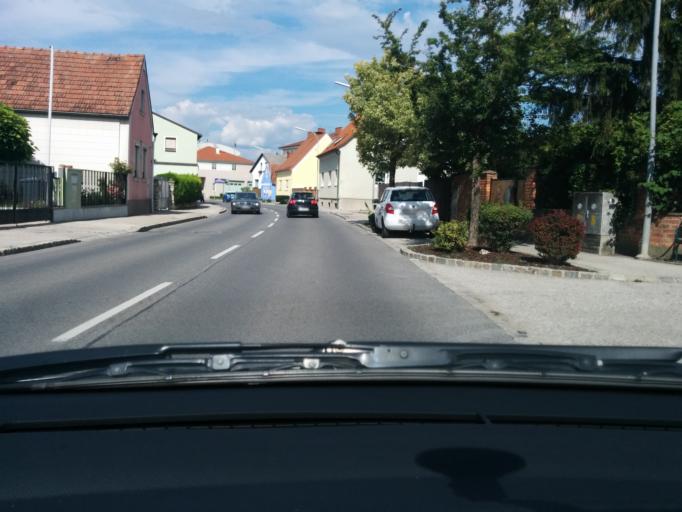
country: AT
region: Lower Austria
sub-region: Politischer Bezirk Wiener Neustadt
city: Zillingdorf
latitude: 47.8514
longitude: 16.3096
